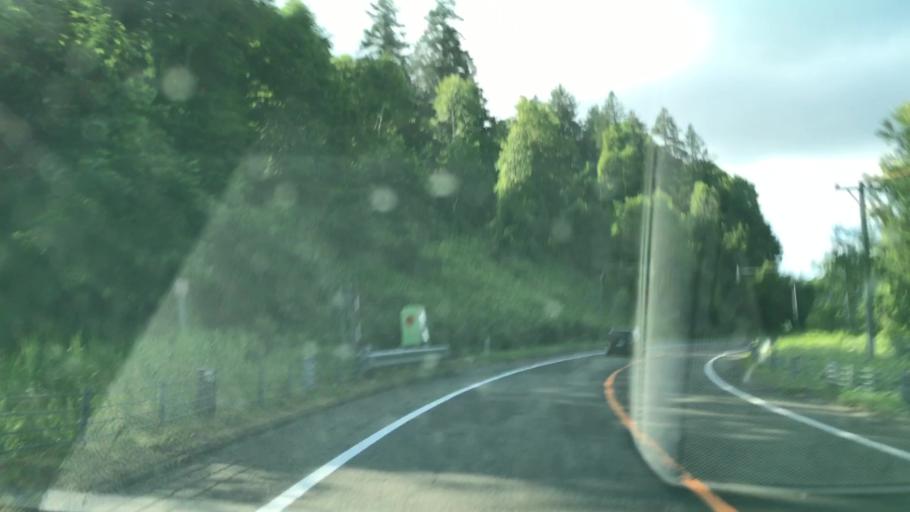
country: JP
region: Hokkaido
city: Shimo-furano
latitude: 42.9103
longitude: 142.4115
